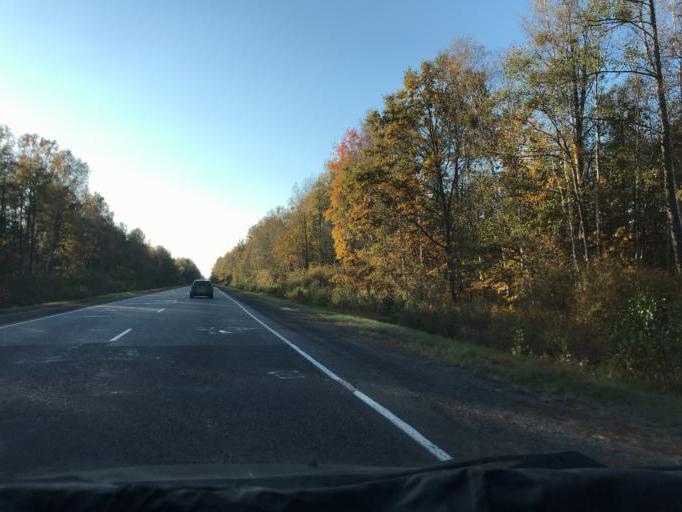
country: BY
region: Gomel
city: Zhytkavichy
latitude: 52.2746
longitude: 28.1696
